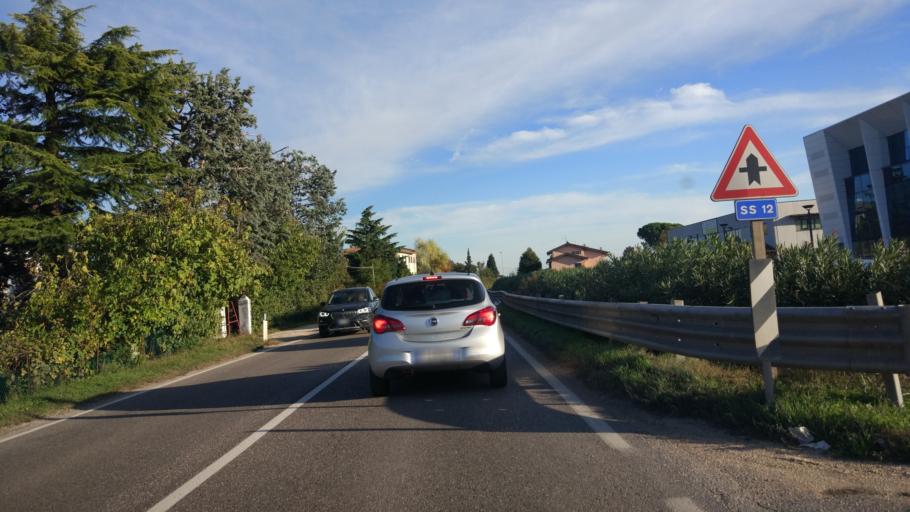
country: IT
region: Veneto
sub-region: Provincia di Verona
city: Ospedaletto
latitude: 45.5016
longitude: 10.8564
